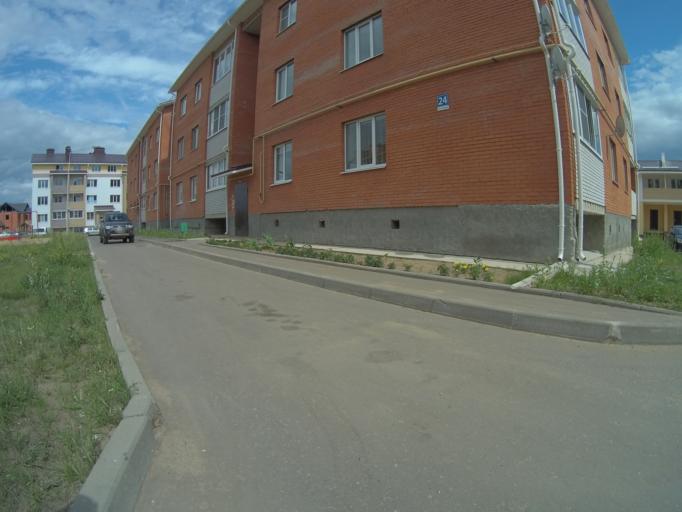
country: RU
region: Vladimir
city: Bogolyubovo
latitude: 56.1993
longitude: 40.5237
